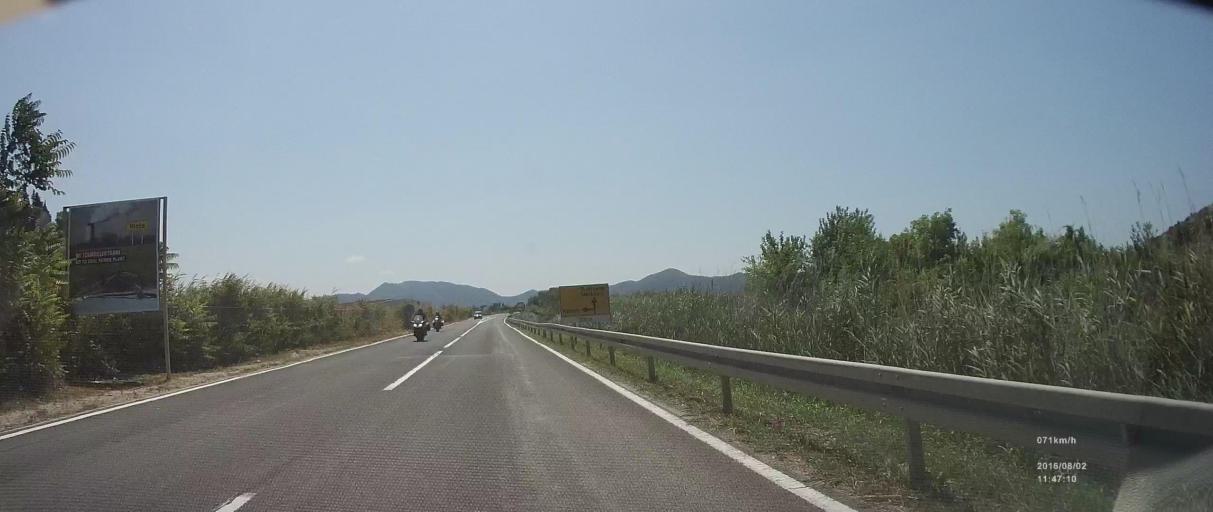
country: HR
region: Dubrovacko-Neretvanska
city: Komin
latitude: 43.0466
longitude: 17.4803
